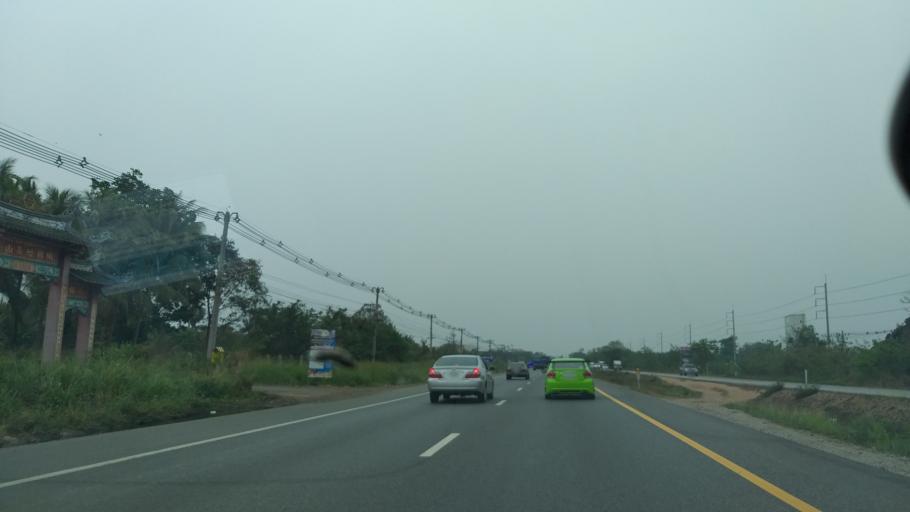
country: TH
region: Chon Buri
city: Ko Chan
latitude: 13.3379
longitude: 101.2705
